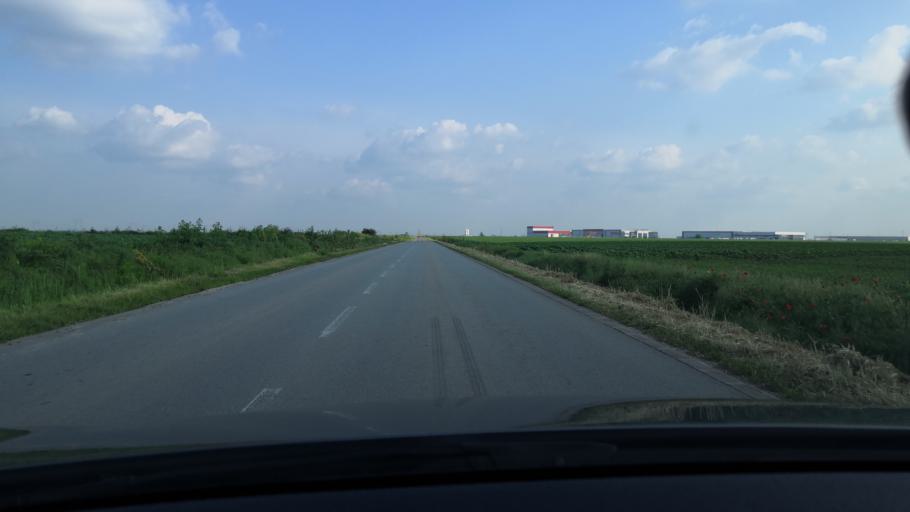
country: RS
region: Autonomna Pokrajina Vojvodina
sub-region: Sremski Okrug
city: Ingija
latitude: 45.0727
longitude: 20.1253
